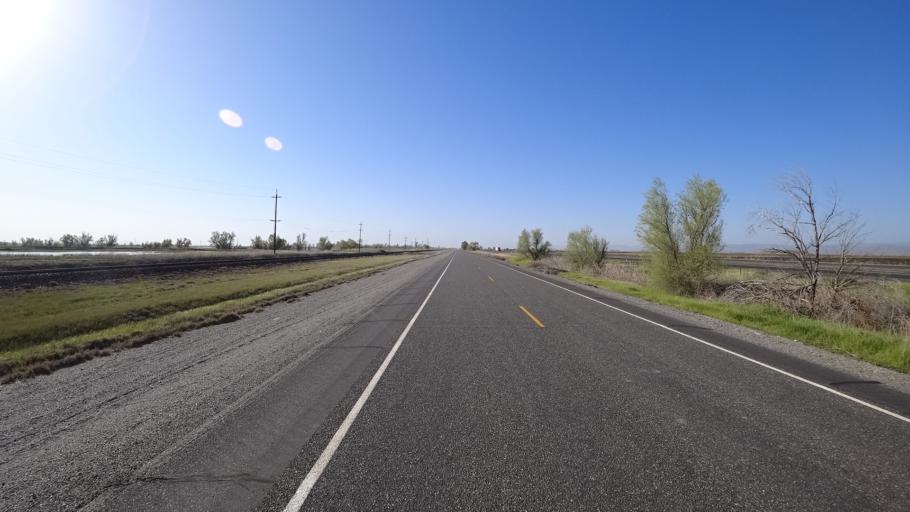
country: US
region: California
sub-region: Glenn County
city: Willows
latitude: 39.4488
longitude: -122.1928
